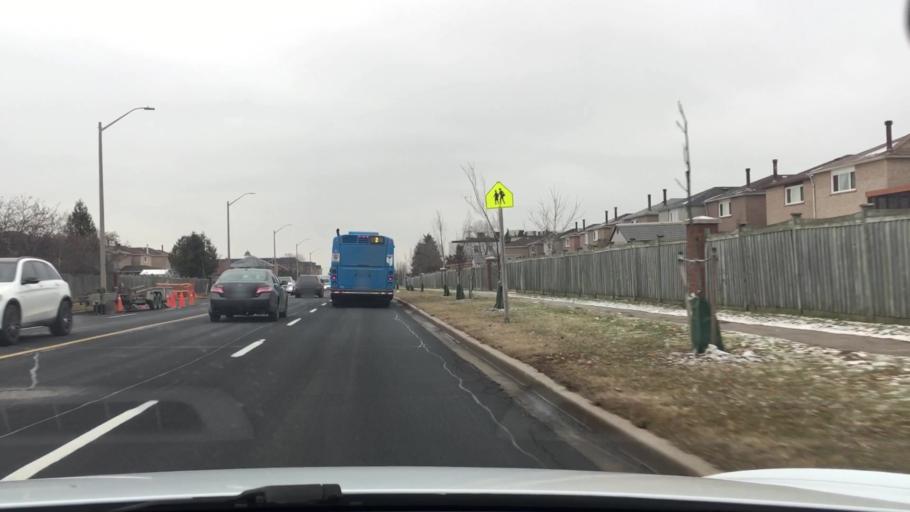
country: CA
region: Ontario
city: Markham
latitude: 43.8421
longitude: -79.2716
